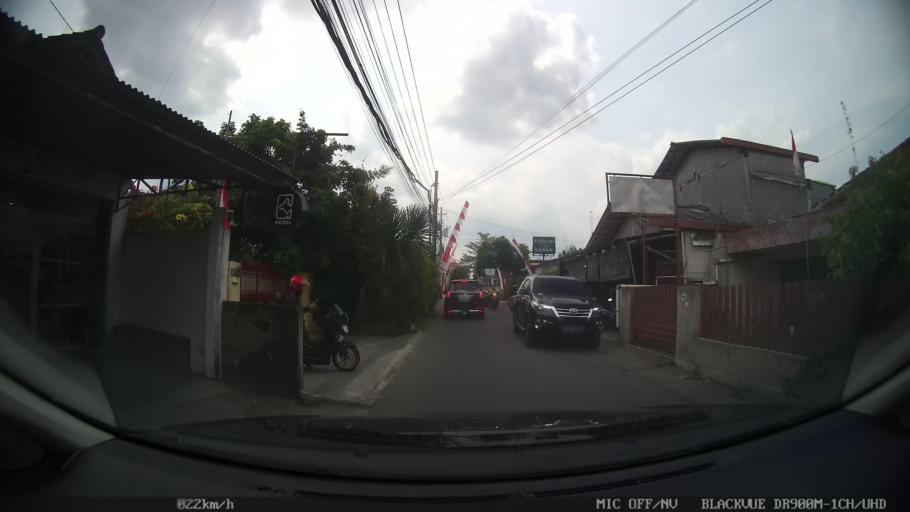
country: ID
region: Daerah Istimewa Yogyakarta
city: Yogyakarta
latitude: -7.7903
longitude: 110.3984
